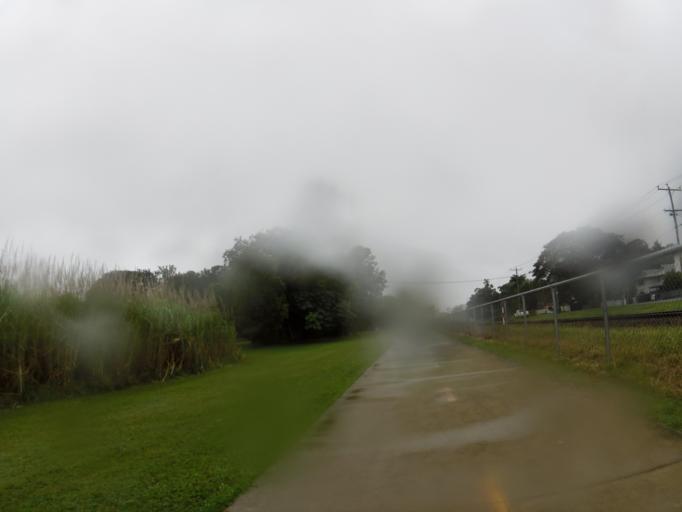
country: AU
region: Queensland
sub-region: Cairns
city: Redlynch
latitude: -16.8784
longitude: 145.7141
